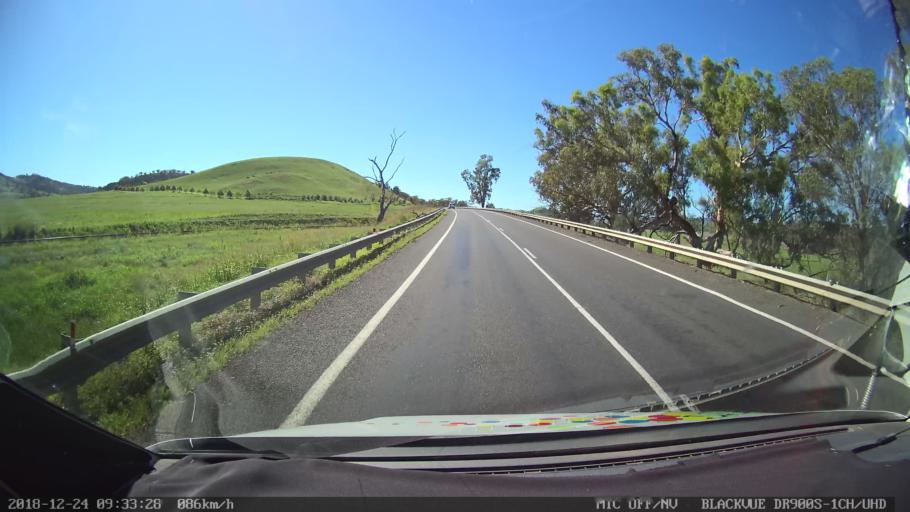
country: AU
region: New South Wales
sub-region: Liverpool Plains
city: Quirindi
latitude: -31.6038
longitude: 150.7076
